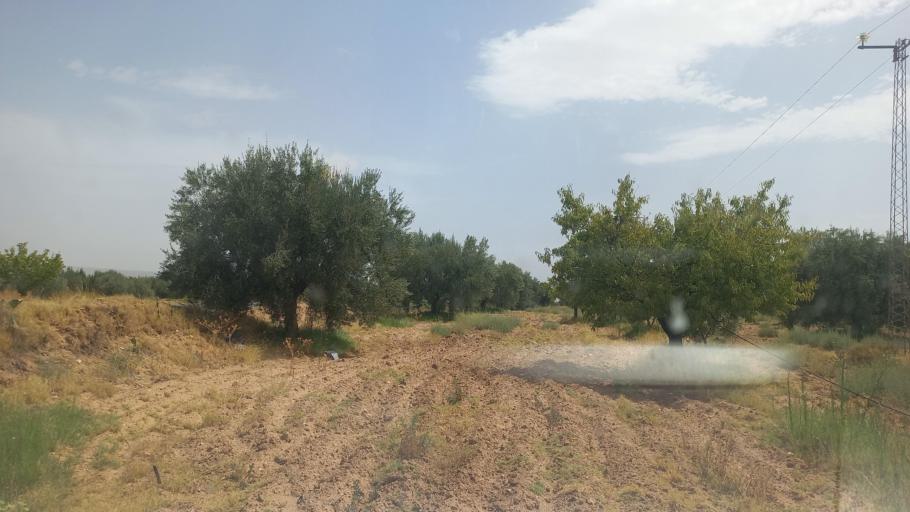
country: TN
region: Al Qasrayn
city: Kasserine
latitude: 35.2647
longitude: 9.0008
